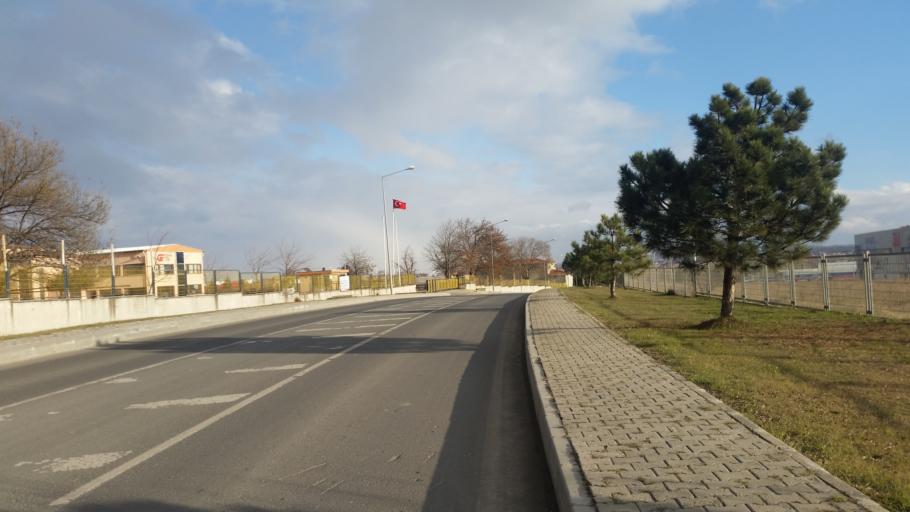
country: TR
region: Tekirdag
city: Cerkezkoey
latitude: 41.2926
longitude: 27.9694
